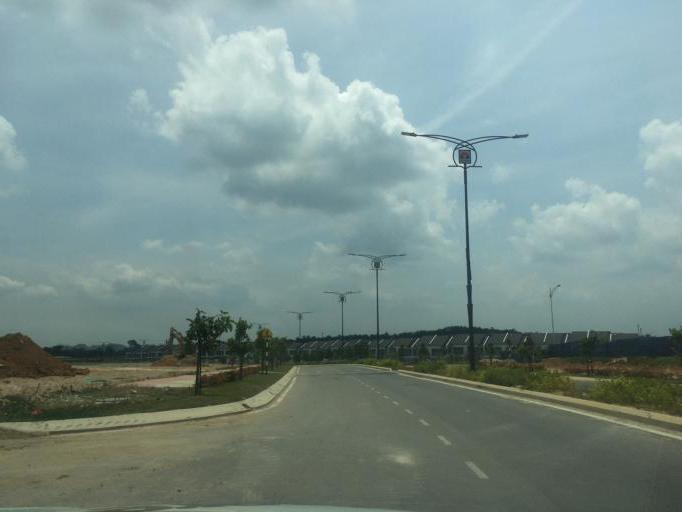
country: MY
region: Putrajaya
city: Putrajaya
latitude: 2.8549
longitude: 101.7052
